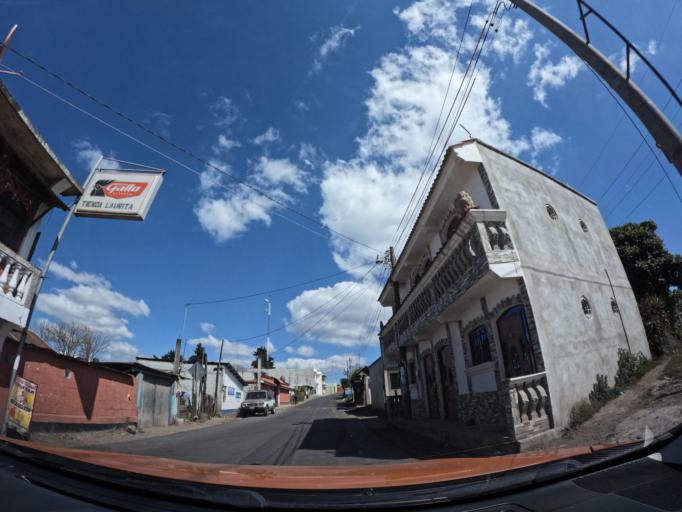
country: GT
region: Chimaltenango
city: Patzun
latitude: 14.6474
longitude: -91.0393
